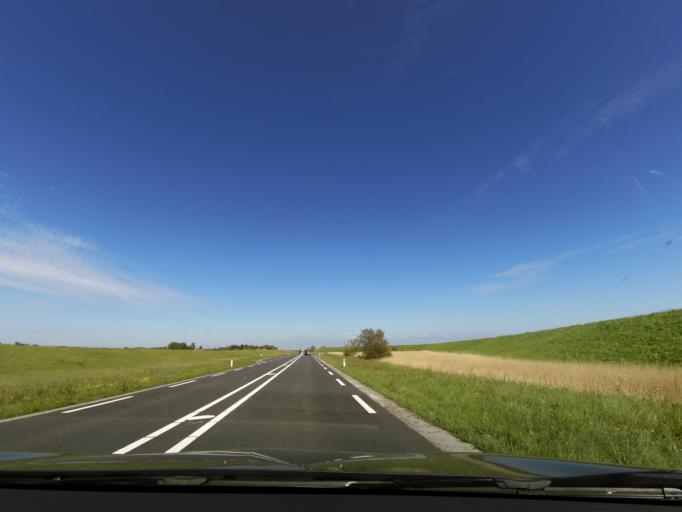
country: NL
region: South Holland
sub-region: Gemeente Goeree-Overflakkee
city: Ouddorp
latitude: 51.7975
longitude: 3.9209
